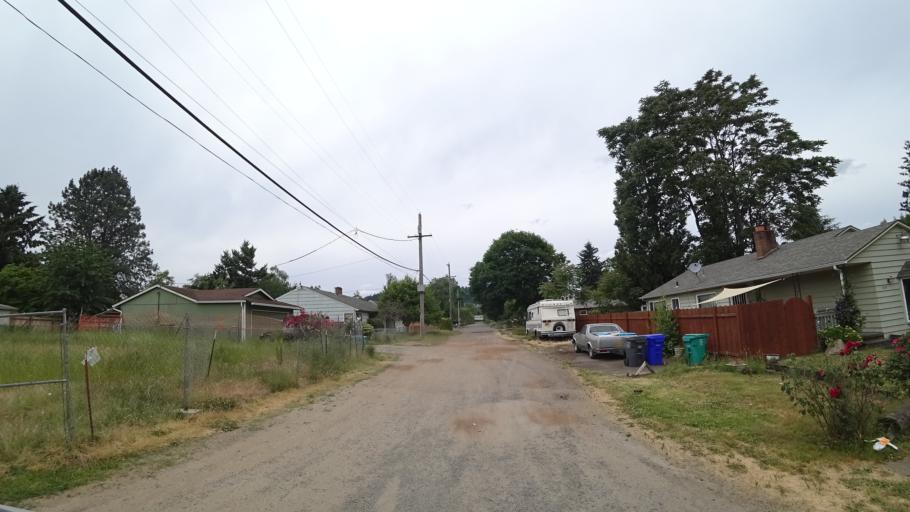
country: US
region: Oregon
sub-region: Multnomah County
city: Lents
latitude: 45.5136
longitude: -122.5742
